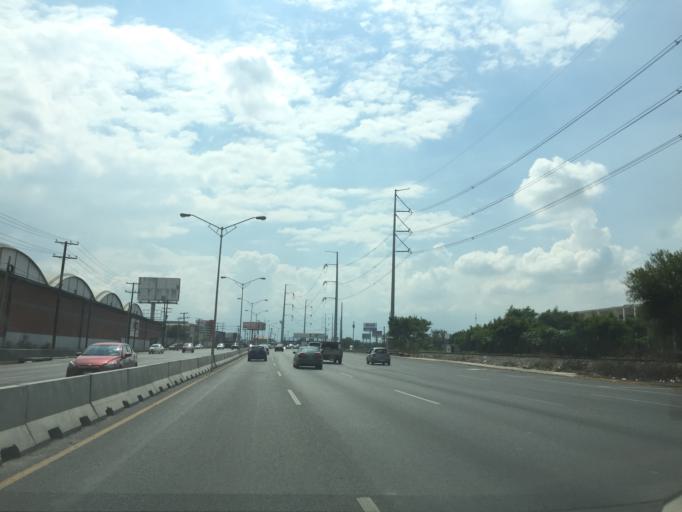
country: MX
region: Nuevo Leon
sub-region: San Nicolas de los Garza
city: San Nicolas de los Garza
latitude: 25.7609
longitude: -100.3060
